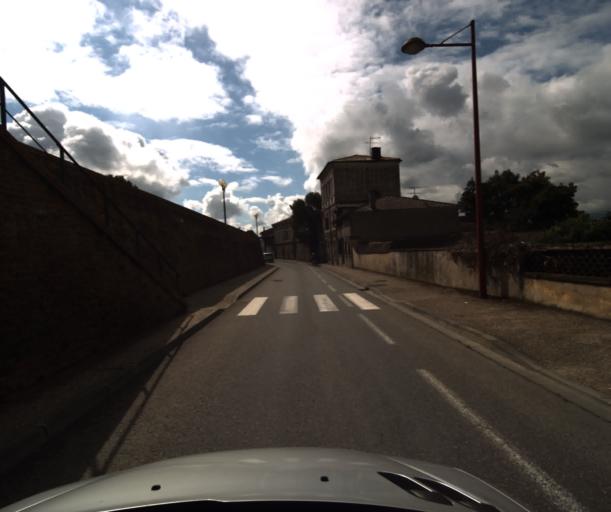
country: FR
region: Midi-Pyrenees
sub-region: Departement du Tarn-et-Garonne
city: Castelsarrasin
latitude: 44.0378
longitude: 1.1052
